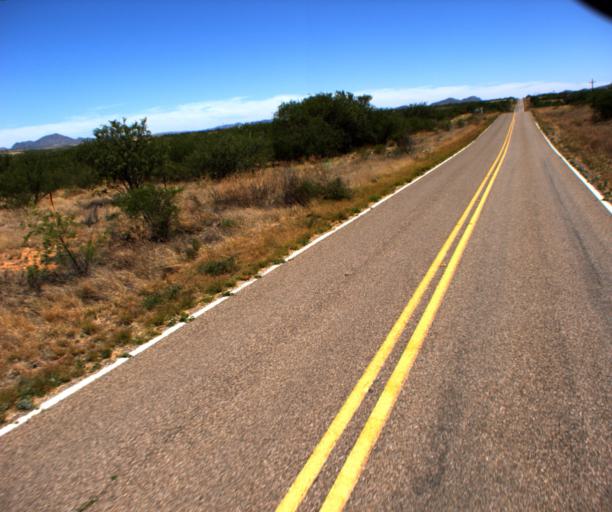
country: US
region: Arizona
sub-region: Pima County
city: Sells
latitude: 31.5640
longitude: -111.5386
